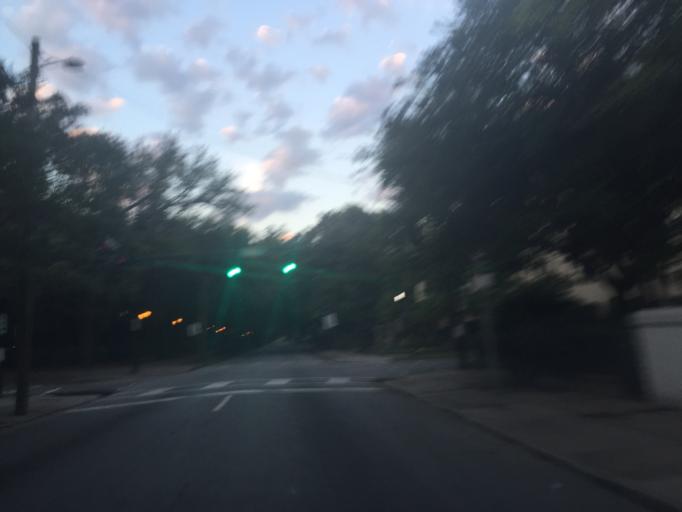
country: US
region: Georgia
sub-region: Chatham County
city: Savannah
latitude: 32.0708
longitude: -81.0962
